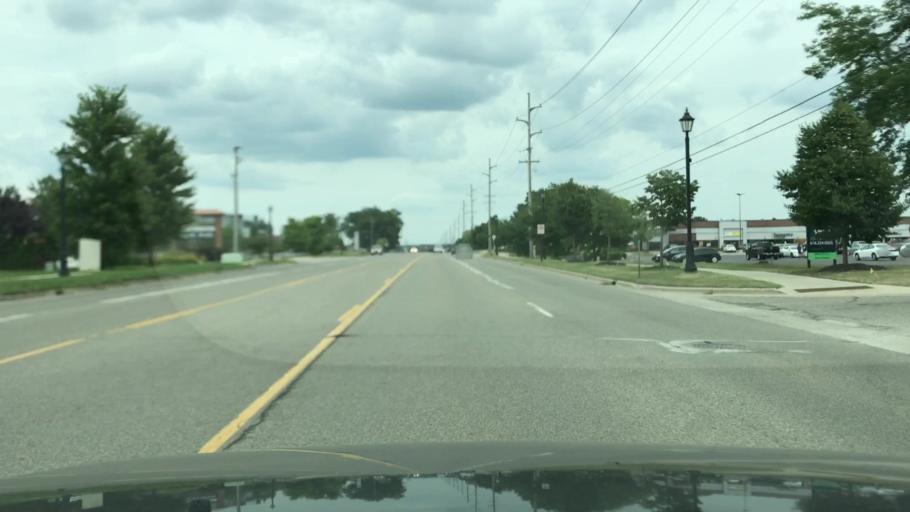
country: US
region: Michigan
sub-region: Kent County
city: Forest Hills
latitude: 42.9131
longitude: -85.5149
